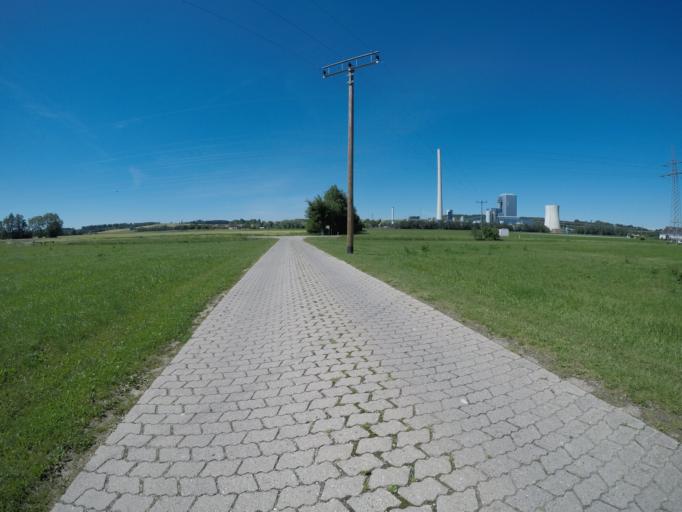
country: DE
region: Bavaria
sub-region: Upper Bavaria
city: Haag an der Amper
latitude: 48.4482
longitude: 11.7990
